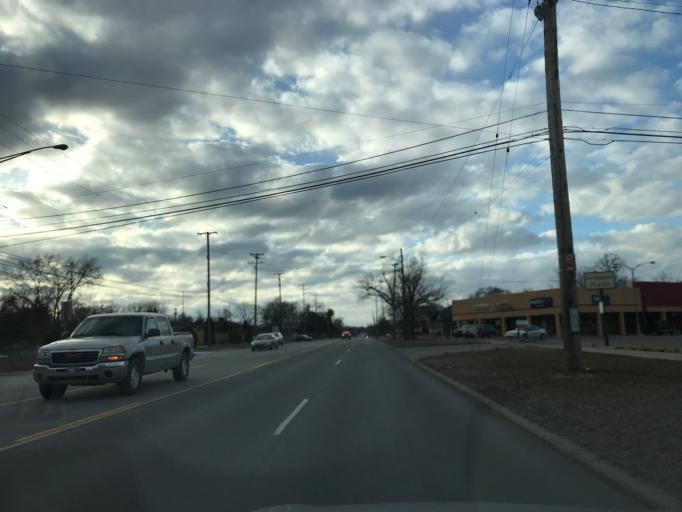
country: US
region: Michigan
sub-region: Oakland County
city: Farmington
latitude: 42.4570
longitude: -83.3577
